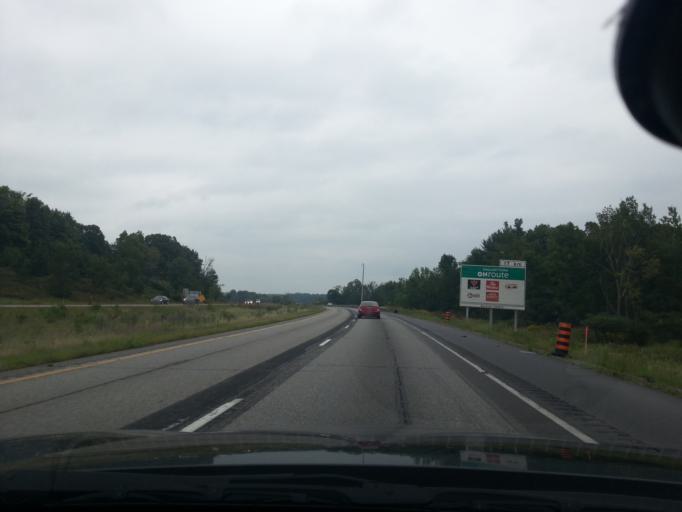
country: US
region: New York
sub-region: Jefferson County
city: Alexandria Bay
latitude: 44.3852
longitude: -75.9689
